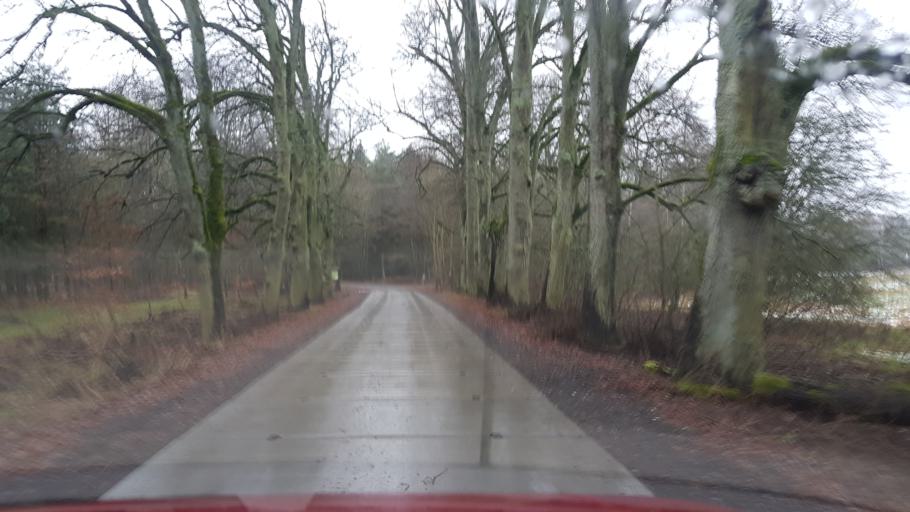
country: PL
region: West Pomeranian Voivodeship
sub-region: Powiat policki
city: Dobra
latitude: 53.5488
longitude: 14.4192
